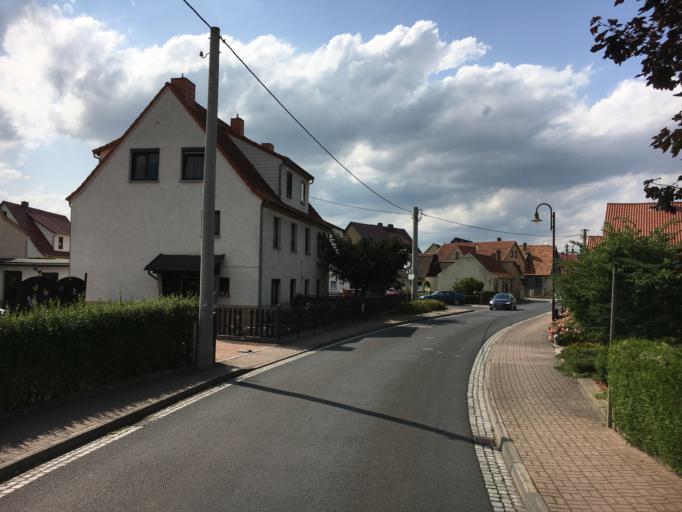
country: DE
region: Thuringia
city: Breitungen
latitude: 50.7626
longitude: 10.3254
